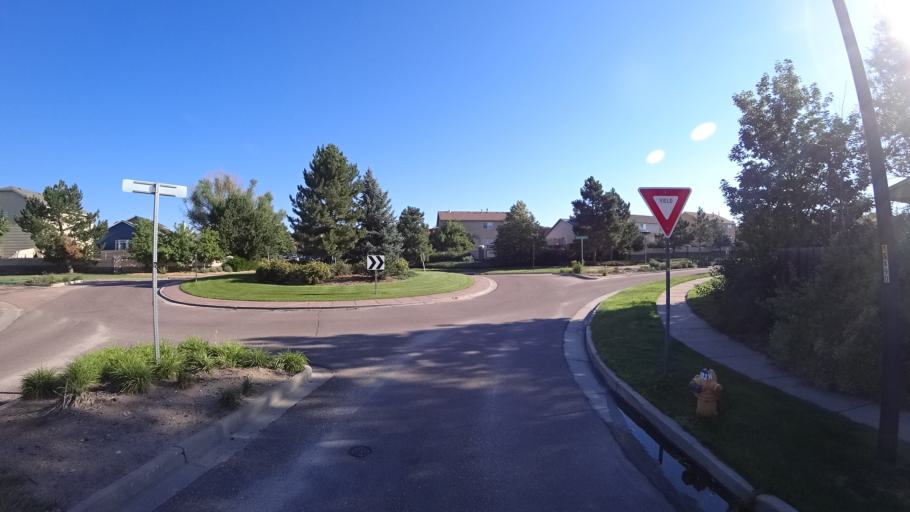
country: US
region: Colorado
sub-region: El Paso County
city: Black Forest
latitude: 38.9636
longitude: -104.7440
